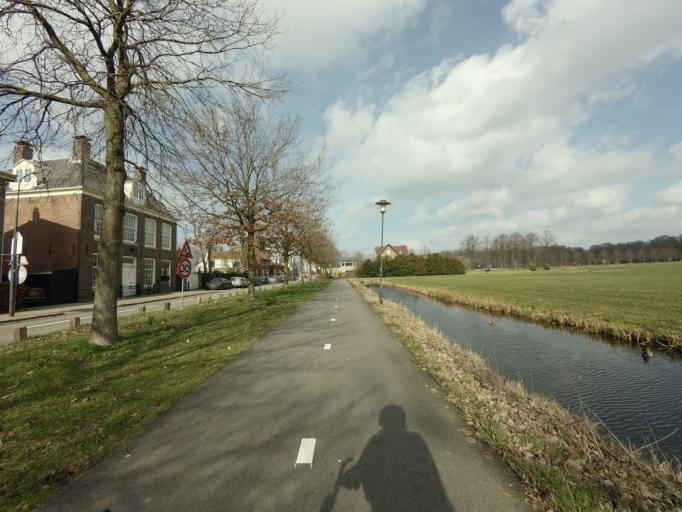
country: NL
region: North Holland
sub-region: Gemeente Wijdemeren
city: Kortenhoef
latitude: 52.2369
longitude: 5.1219
